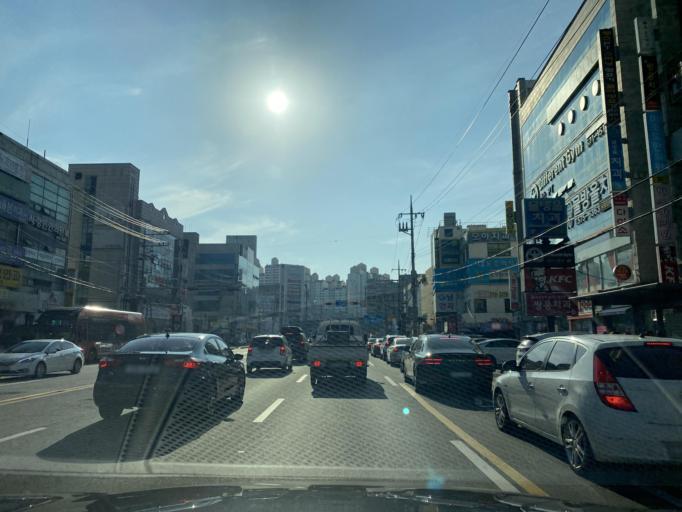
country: KR
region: Chungcheongnam-do
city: Cheonan
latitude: 36.7966
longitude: 127.1291
